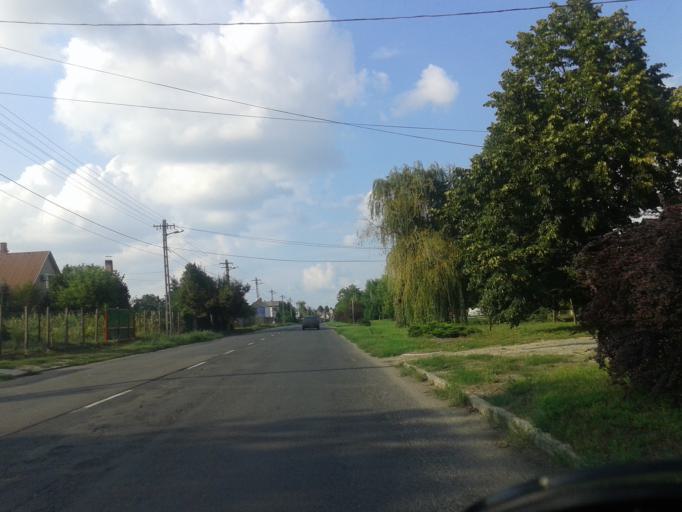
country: HU
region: Pest
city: Kiskunlachaza
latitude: 47.1735
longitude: 19.0003
